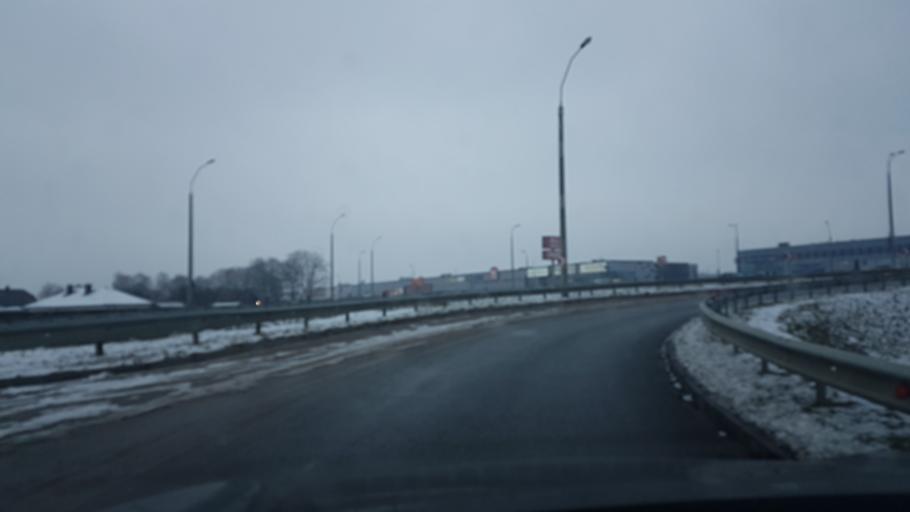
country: BY
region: Minsk
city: Bal'shavik
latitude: 53.9705
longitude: 27.5403
